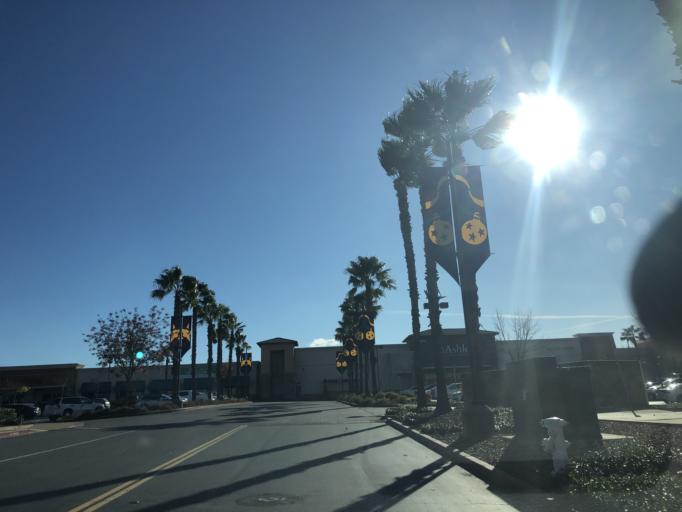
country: US
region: California
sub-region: Placer County
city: Roseville
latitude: 38.7898
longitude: -121.2843
